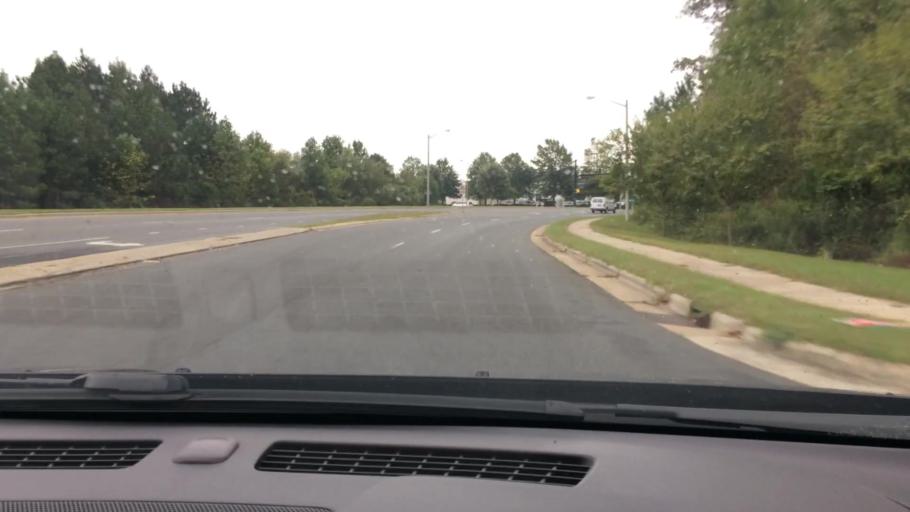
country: US
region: North Carolina
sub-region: Pitt County
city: Summerfield
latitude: 35.6115
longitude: -77.4103
